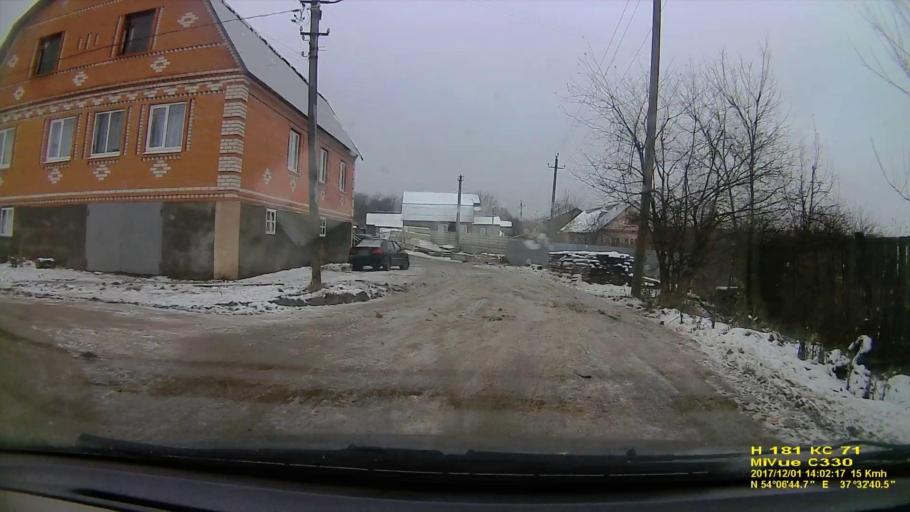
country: RU
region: Tula
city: Kosaya Gora
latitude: 54.1124
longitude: 37.5445
